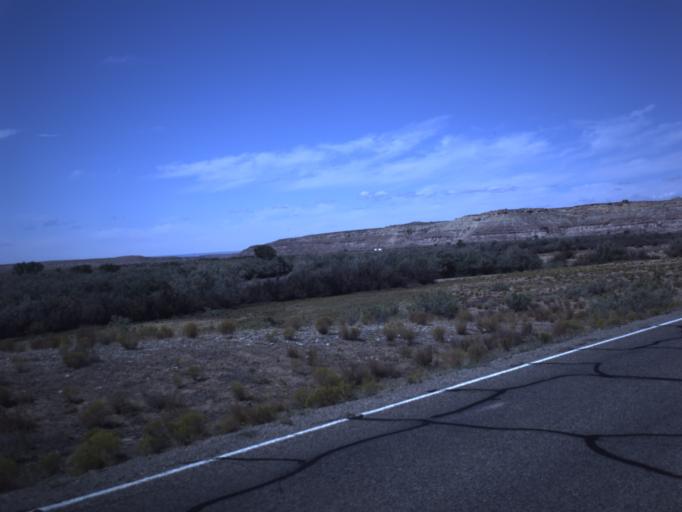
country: US
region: Utah
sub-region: San Juan County
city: Blanding
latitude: 37.2472
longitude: -109.2547
